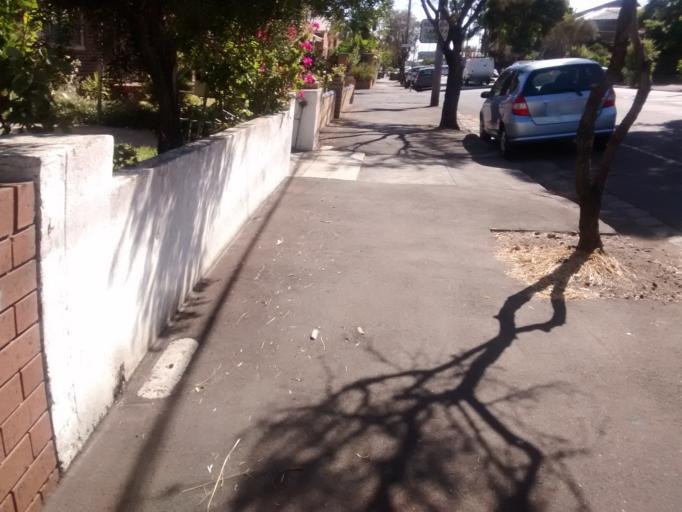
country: AU
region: Victoria
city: Brunswick East
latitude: -37.7738
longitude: 144.9811
